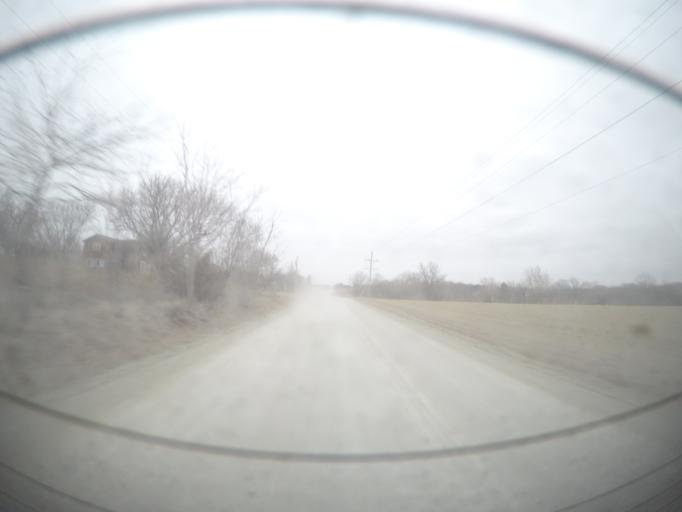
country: US
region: Kansas
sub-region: Wabaunsee County
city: Alma
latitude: 39.0803
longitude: -96.2424
